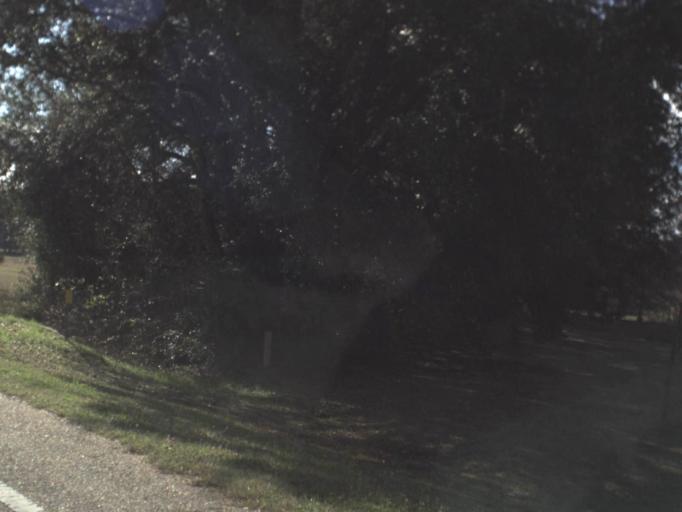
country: US
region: Florida
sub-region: Jackson County
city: Malone
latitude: 30.9882
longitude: -85.1891
